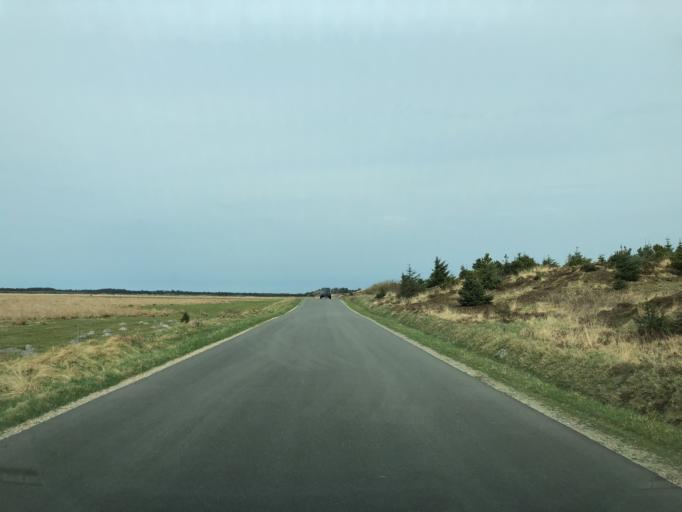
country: DK
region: South Denmark
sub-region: Varde Kommune
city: Oksbol
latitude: 55.6452
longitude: 8.1780
